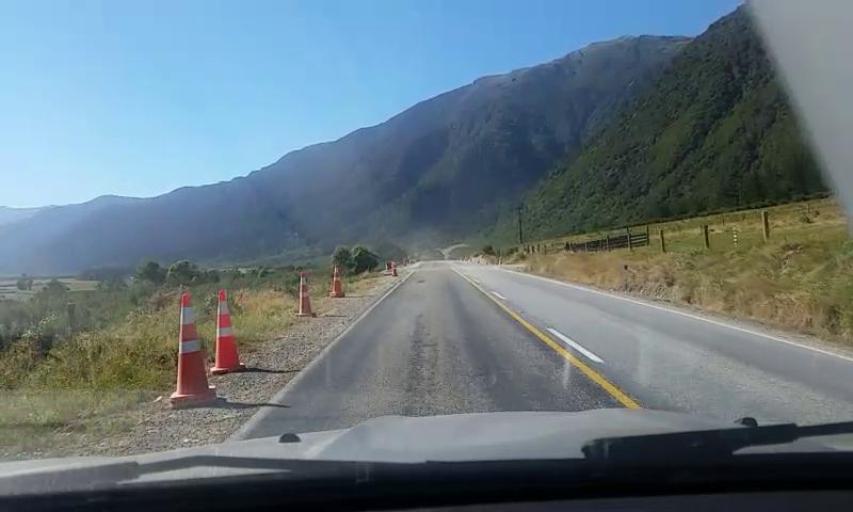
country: NZ
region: West Coast
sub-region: Grey District
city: Greymouth
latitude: -42.7486
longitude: 171.5399
